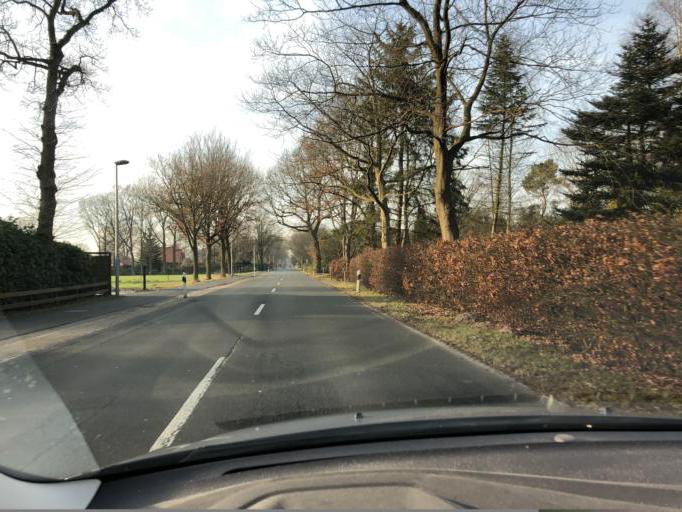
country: DE
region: Lower Saxony
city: Bad Zwischenahn
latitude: 53.1443
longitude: 8.0966
